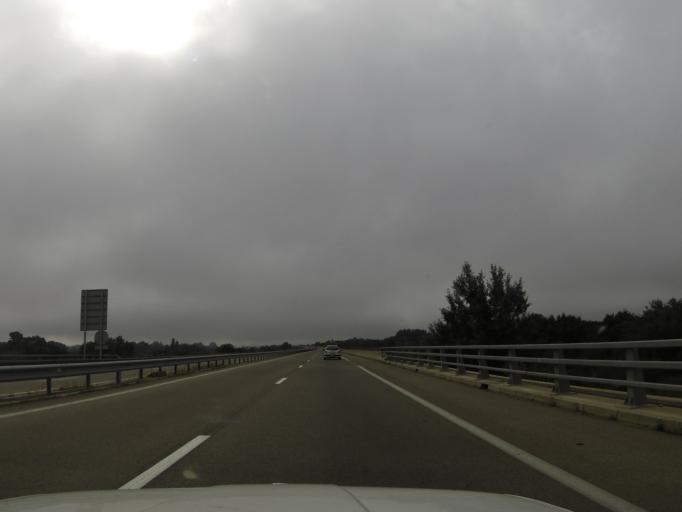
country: FR
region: Languedoc-Roussillon
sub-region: Departement du Gard
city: Saint-Genies-de-Malgoires
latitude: 43.9598
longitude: 4.2306
